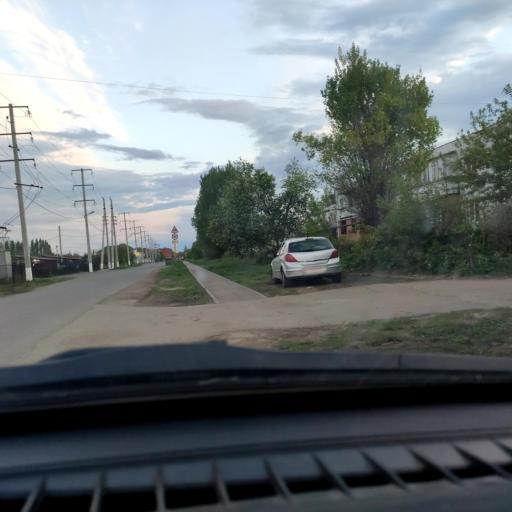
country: RU
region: Samara
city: Podstepki
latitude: 53.5194
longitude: 49.1128
